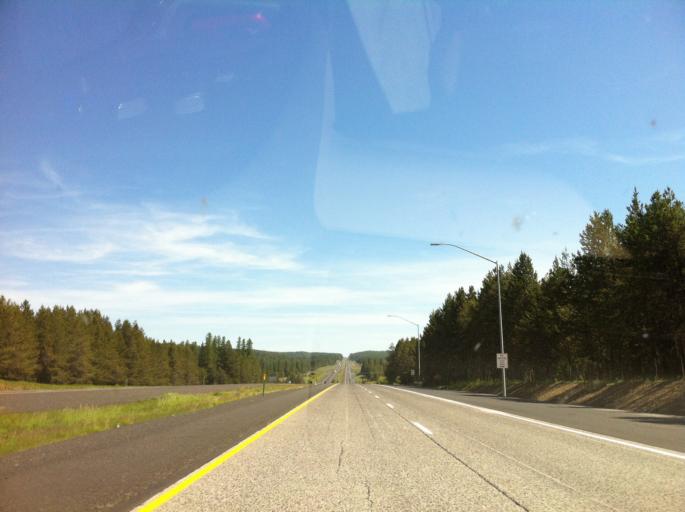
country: US
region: Oregon
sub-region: Umatilla County
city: Mission
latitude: 45.5203
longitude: -118.4390
